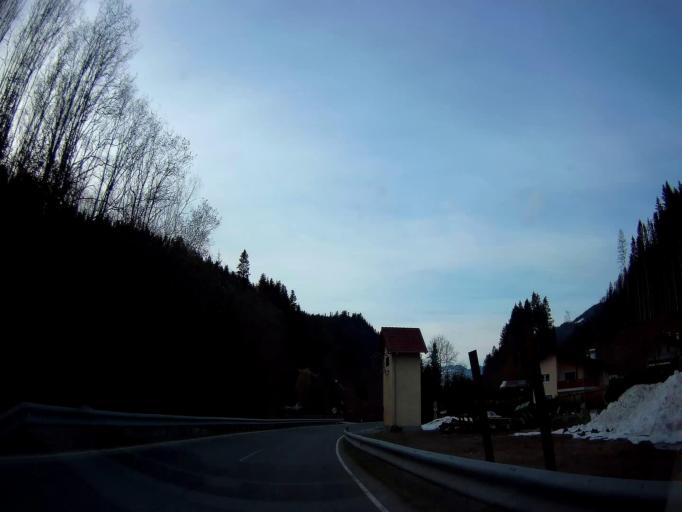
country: AT
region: Salzburg
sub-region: Politischer Bezirk Hallein
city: Abtenau
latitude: 47.5329
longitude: 13.4245
